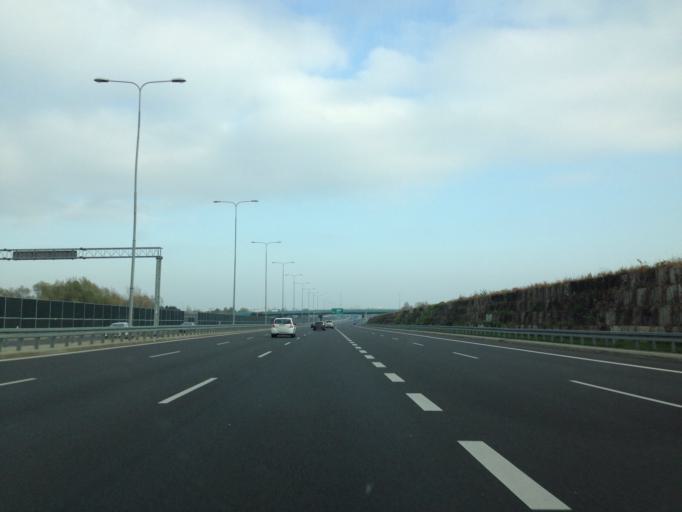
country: PL
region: Masovian Voivodeship
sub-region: Powiat piaseczynski
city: Mysiadlo
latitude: 52.1391
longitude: 21.0008
